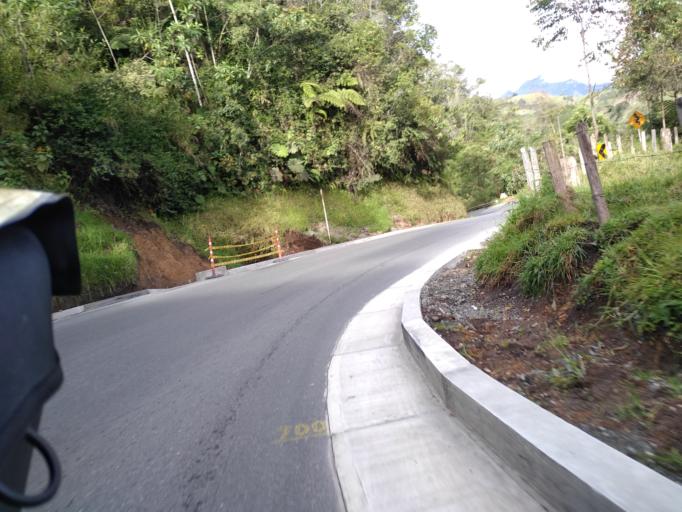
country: CO
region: Tolima
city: Herveo
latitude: 5.1378
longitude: -75.1833
